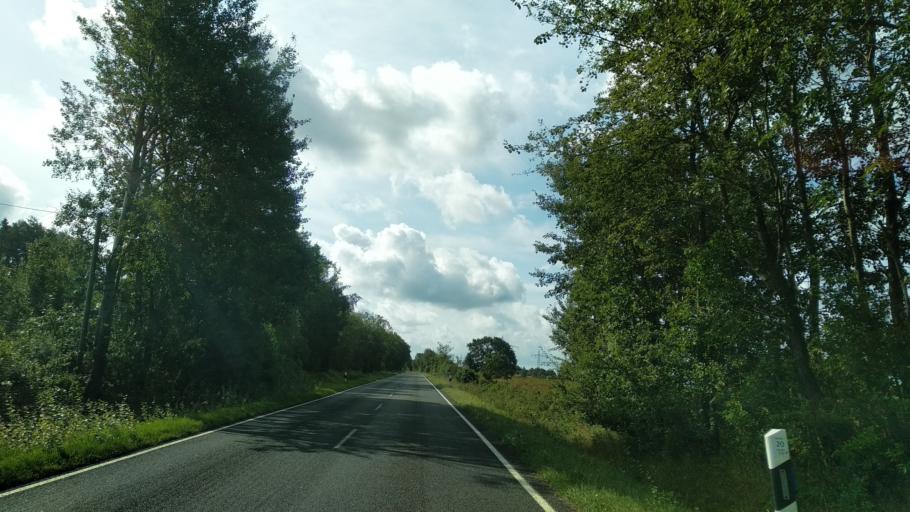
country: DE
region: Schleswig-Holstein
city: Lottorf
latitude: 54.4466
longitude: 9.5943
